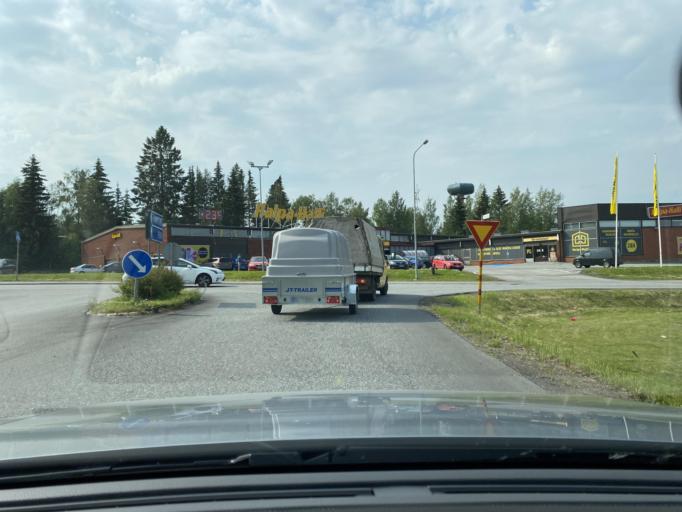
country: FI
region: Pirkanmaa
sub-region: Luoteis-Pirkanmaa
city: Parkano
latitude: 62.0055
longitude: 23.0110
